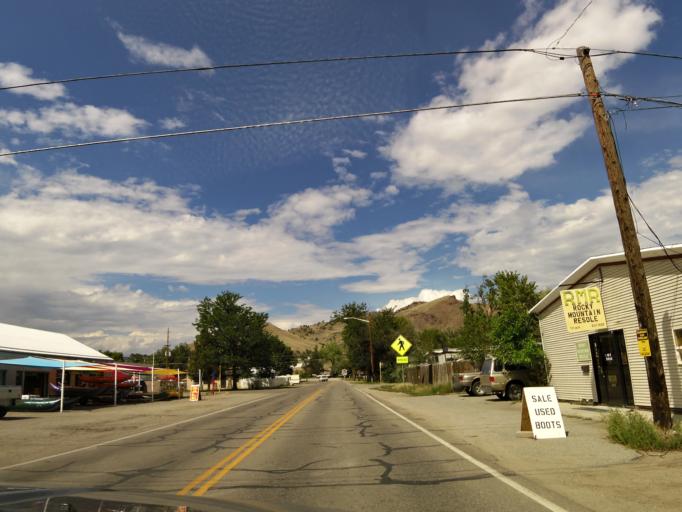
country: US
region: Colorado
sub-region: Chaffee County
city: Salida
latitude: 38.5305
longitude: -105.9847
